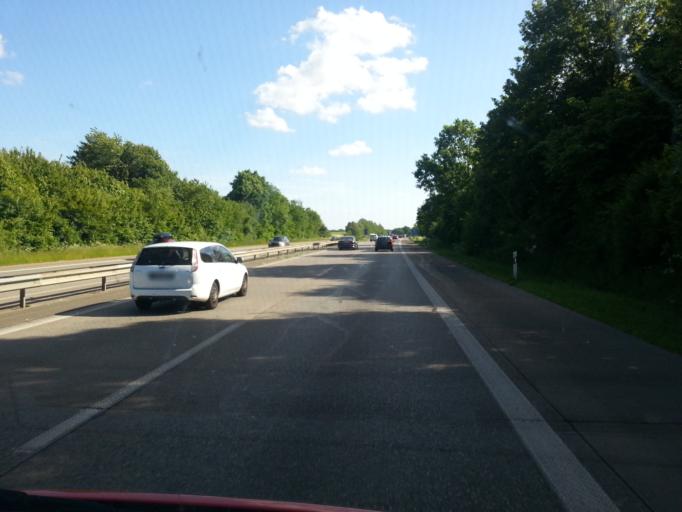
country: DE
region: Schleswig-Holstein
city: Scharbeutz
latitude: 54.0208
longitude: 10.7309
